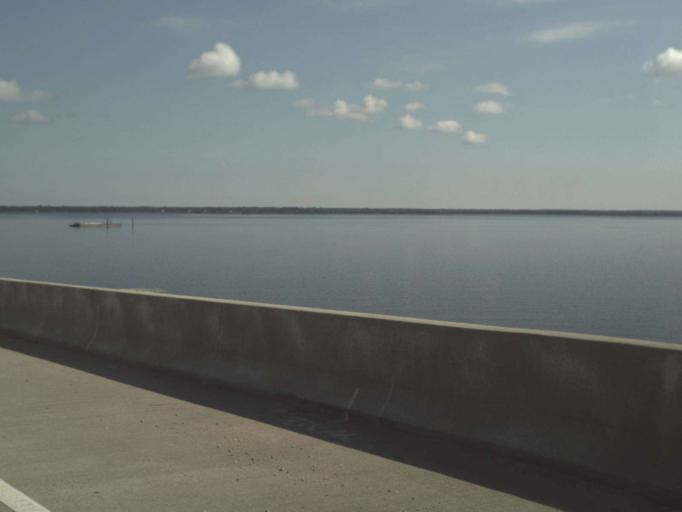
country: US
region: Florida
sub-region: Walton County
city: Seaside
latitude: 30.4018
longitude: -86.1680
